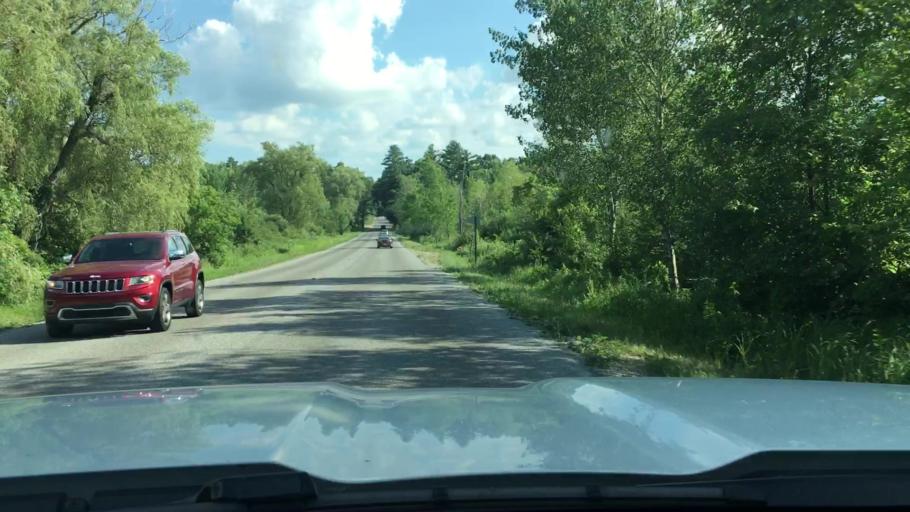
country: US
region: Michigan
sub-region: Montcalm County
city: Greenville
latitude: 43.1612
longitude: -85.3527
